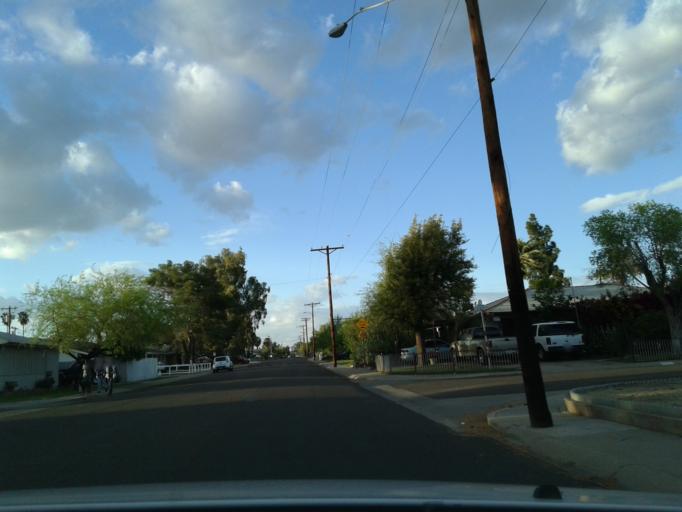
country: US
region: Arizona
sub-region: Maricopa County
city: Glendale
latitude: 33.5441
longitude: -112.1039
